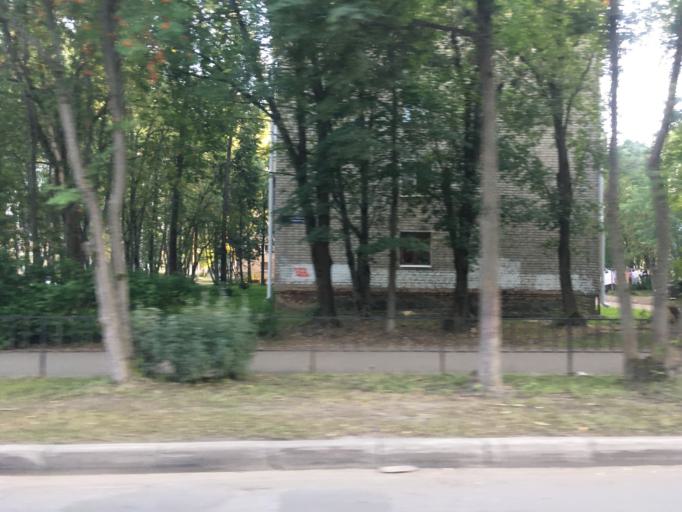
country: RU
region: Mariy-El
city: Yoshkar-Ola
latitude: 56.6477
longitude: 47.8819
